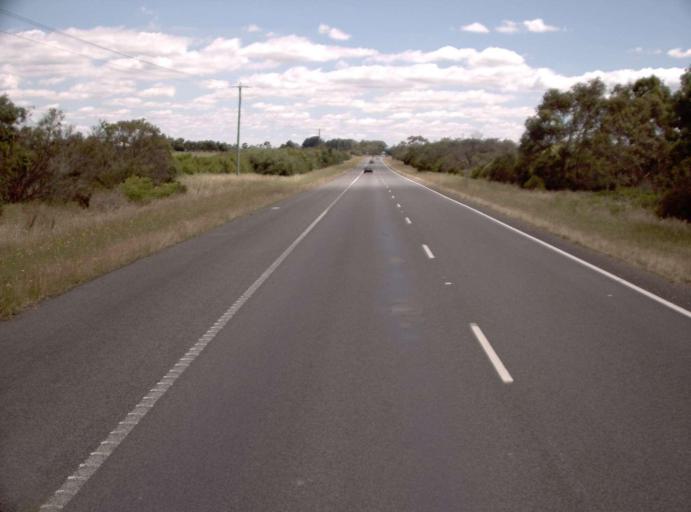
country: AU
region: Victoria
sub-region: Cardinia
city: Koo-Wee-Rup
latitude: -38.2998
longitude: 145.5433
